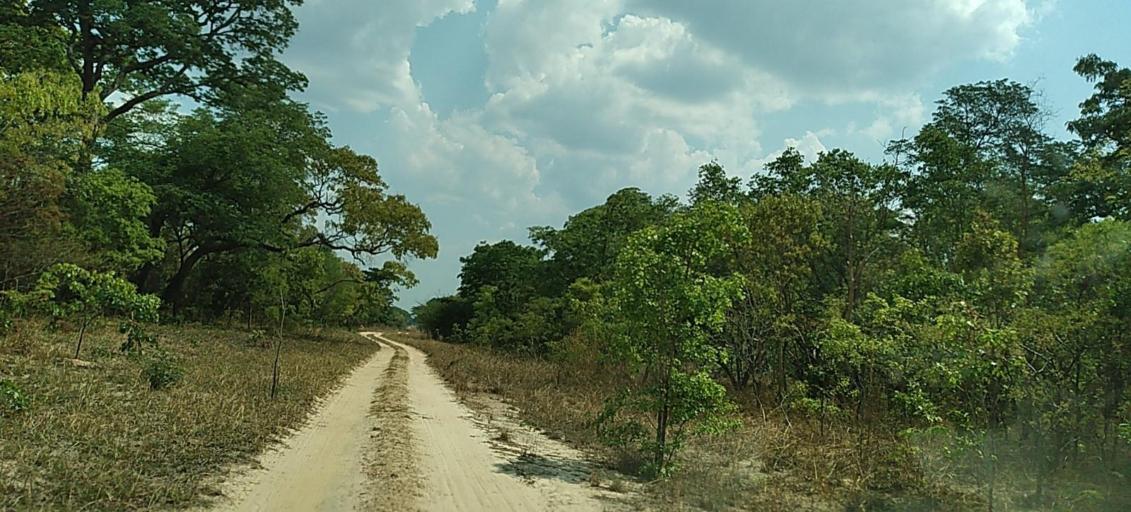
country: ZM
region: Copperbelt
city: Mpongwe
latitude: -13.8306
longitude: 27.9399
